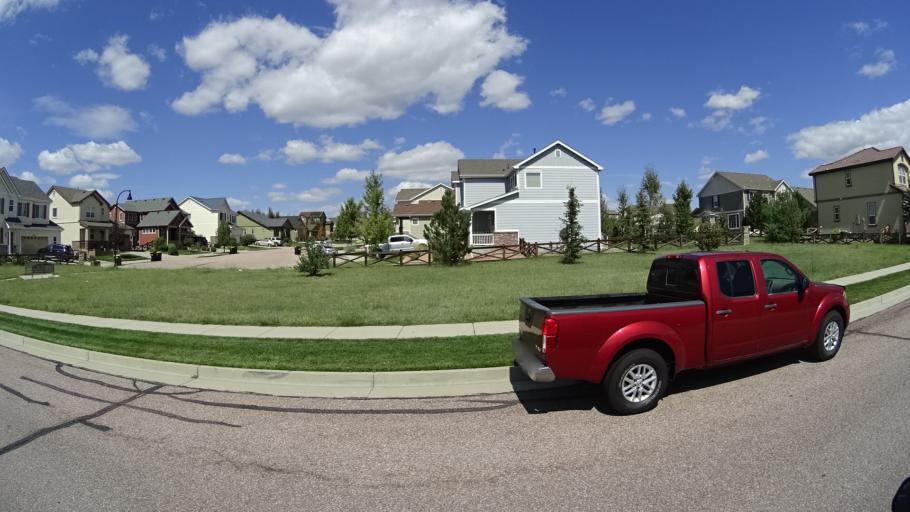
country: US
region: Colorado
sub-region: El Paso County
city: Cimarron Hills
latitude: 38.9278
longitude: -104.6768
